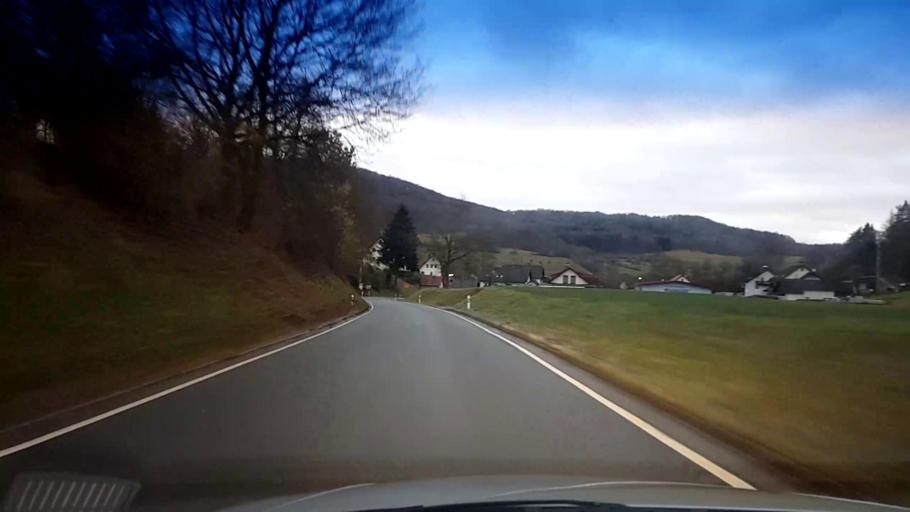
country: DE
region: Bavaria
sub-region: Upper Franconia
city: Schesslitz
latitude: 50.0146
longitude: 11.0697
